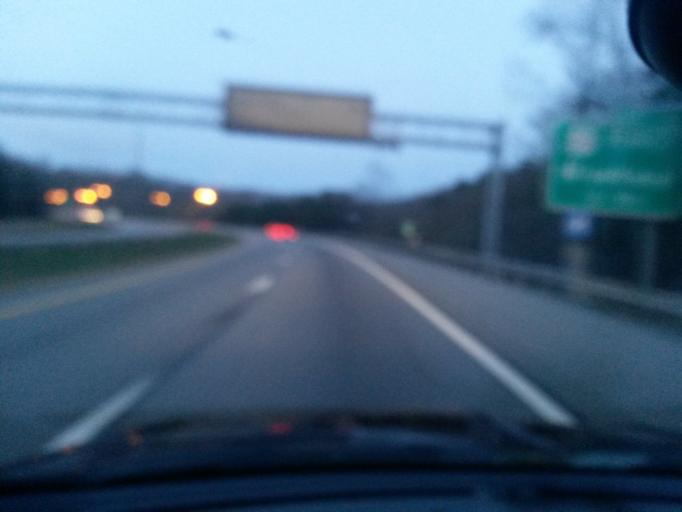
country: US
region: West Virginia
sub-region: Mercer County
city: Princeton
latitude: 37.2916
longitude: -81.1220
